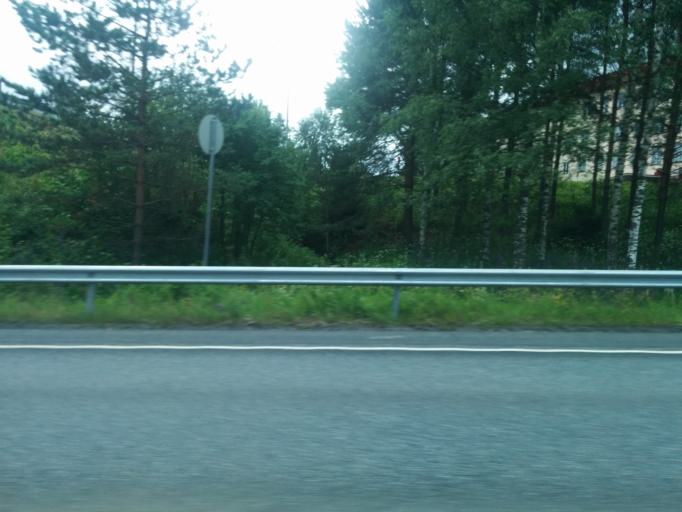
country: FI
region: Pirkanmaa
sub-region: Tampere
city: Orivesi
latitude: 61.6849
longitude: 24.3577
